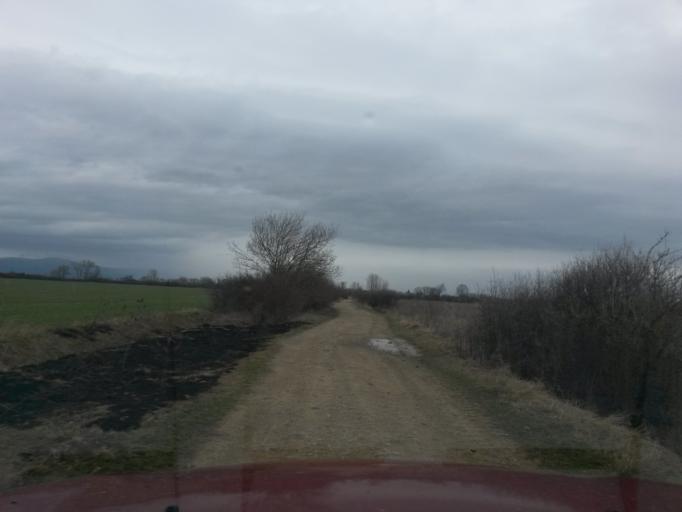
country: SK
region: Kosicky
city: Michalovce
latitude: 48.6965
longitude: 21.9060
